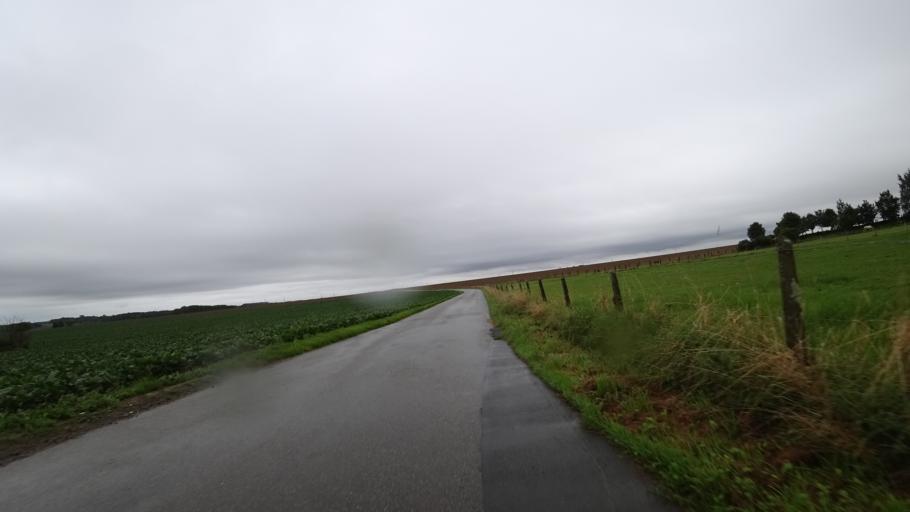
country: BE
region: Wallonia
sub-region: Province de Namur
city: Namur
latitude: 50.5277
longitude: 4.7974
